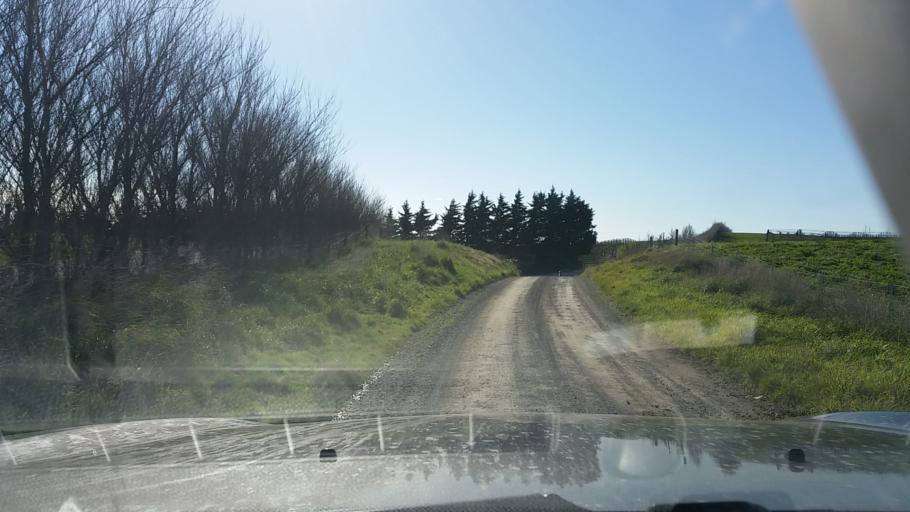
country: NZ
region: Marlborough
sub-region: Marlborough District
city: Blenheim
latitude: -41.6631
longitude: 174.1368
